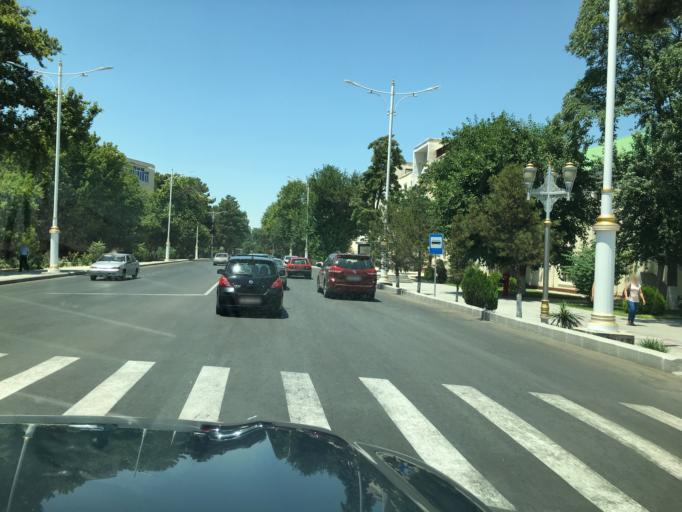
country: TM
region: Ahal
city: Ashgabat
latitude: 37.9361
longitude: 58.3895
